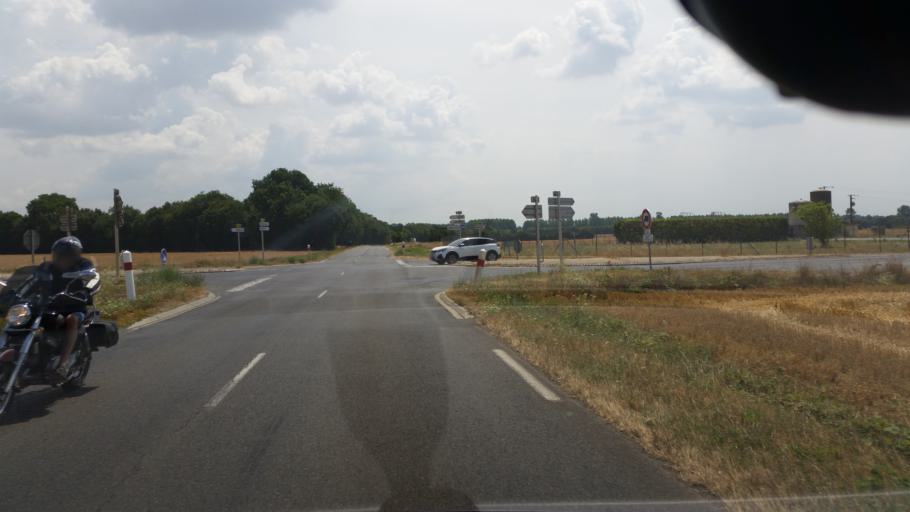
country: FR
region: Poitou-Charentes
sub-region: Departement de la Charente-Maritime
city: Courcon
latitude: 46.1757
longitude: -0.8450
